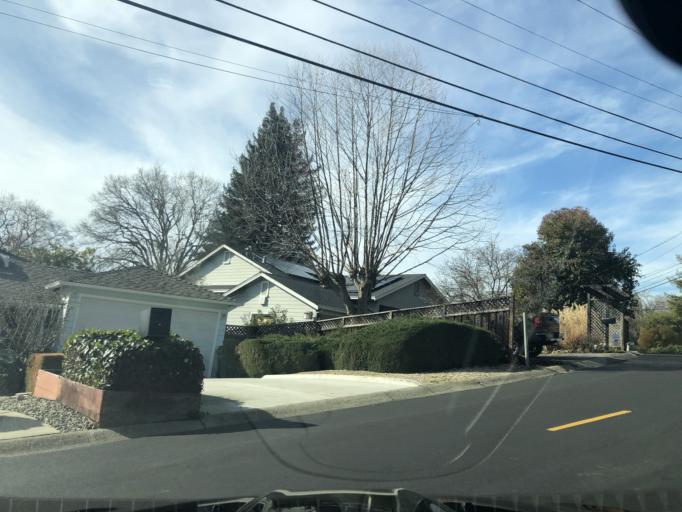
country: US
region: California
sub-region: Contra Costa County
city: Saranap
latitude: 37.8912
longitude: -122.0833
